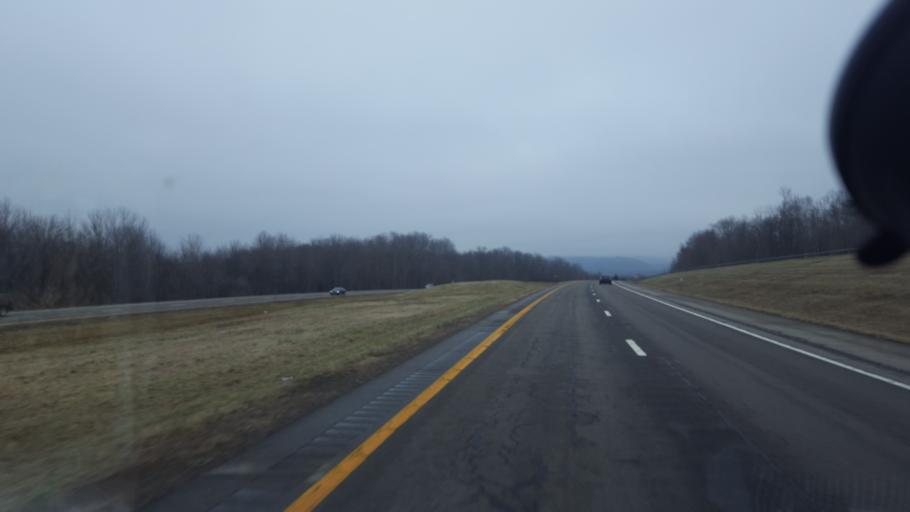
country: US
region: New York
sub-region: Cattaraugus County
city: Randolph
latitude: 42.1625
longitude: -79.0079
